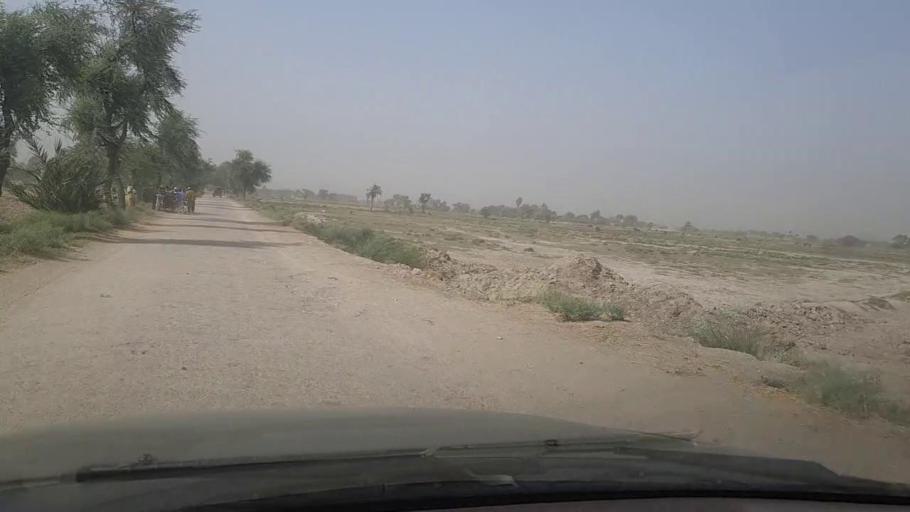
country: PK
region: Sindh
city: Shikarpur
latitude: 27.9268
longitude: 68.6151
